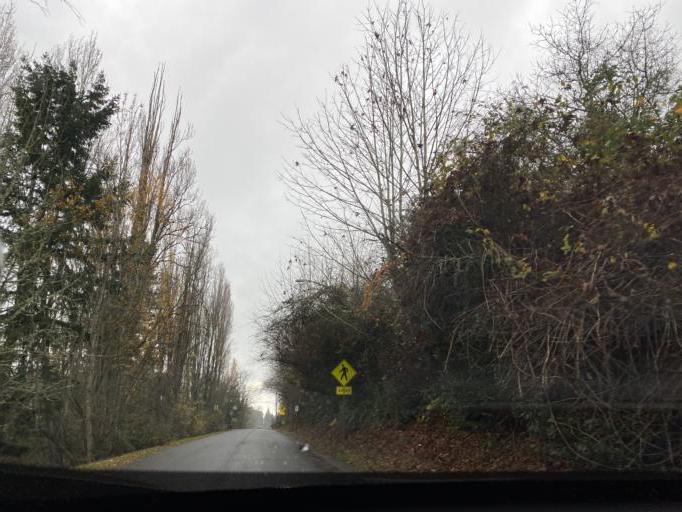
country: US
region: Washington
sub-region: King County
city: Mercer Island
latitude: 47.5913
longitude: -122.2269
